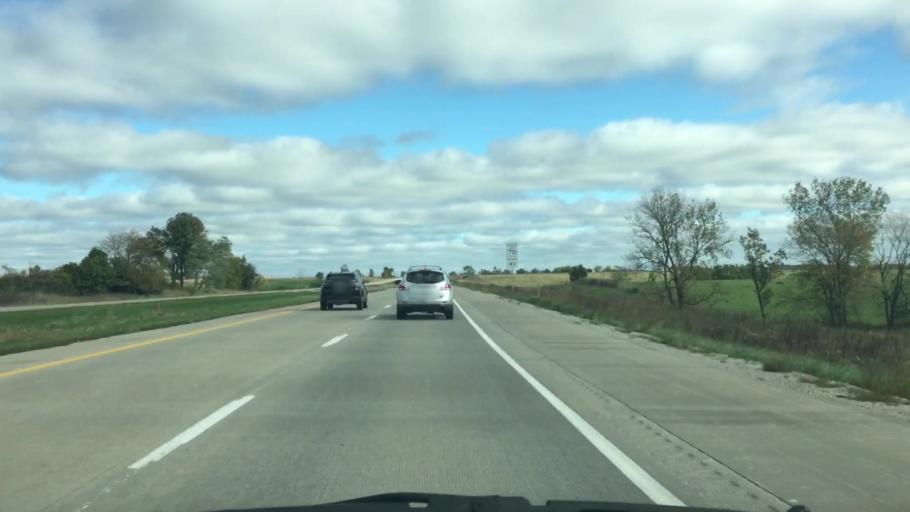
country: US
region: Iowa
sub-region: Decatur County
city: Leon
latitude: 40.8209
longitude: -93.8220
